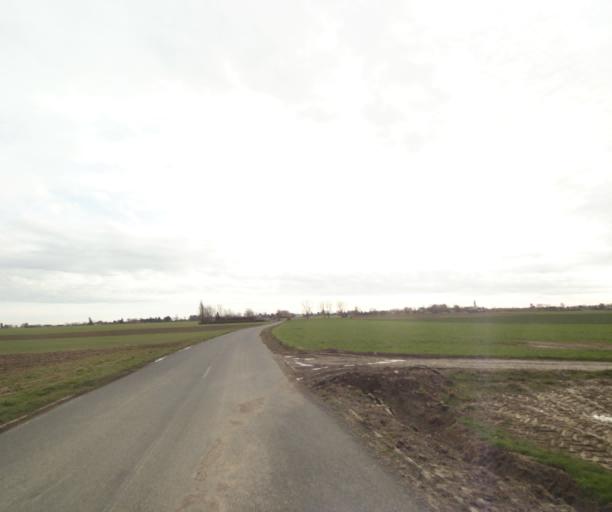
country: FR
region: Nord-Pas-de-Calais
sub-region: Departement du Nord
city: Quarouble
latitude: 50.3737
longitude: 3.6364
